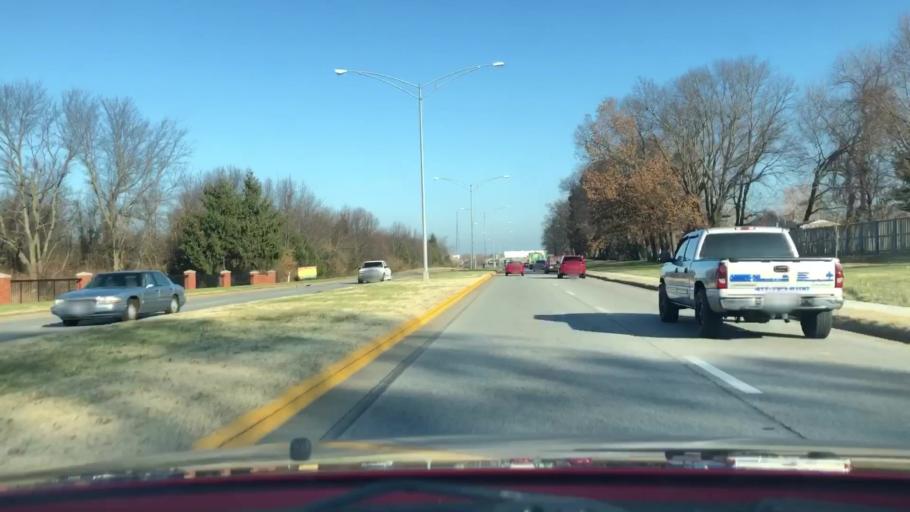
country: US
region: Missouri
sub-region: Greene County
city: Battlefield
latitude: 37.1486
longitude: -93.3191
